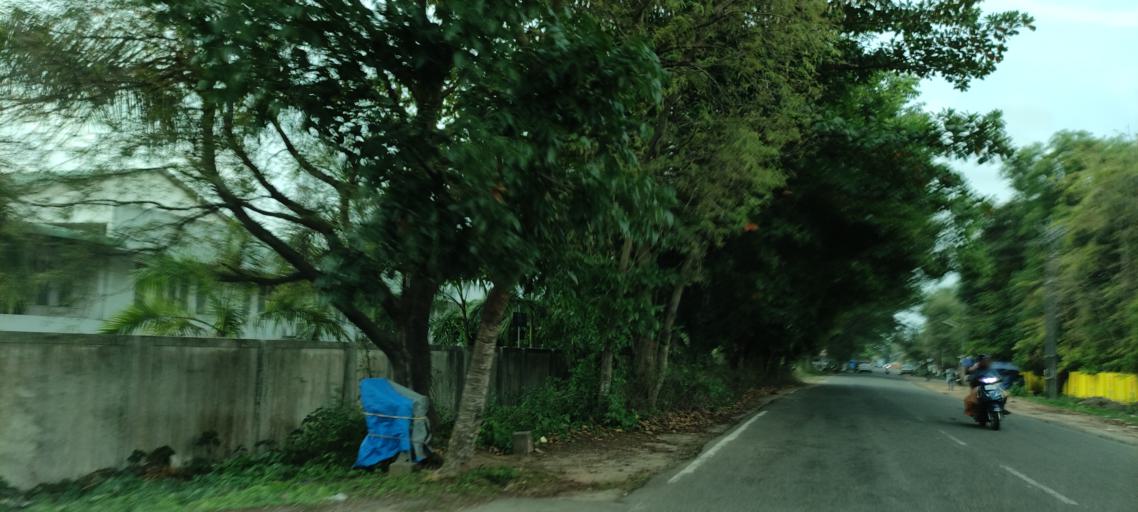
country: IN
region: Kerala
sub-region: Kottayam
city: Vaikam
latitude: 9.7487
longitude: 76.3634
